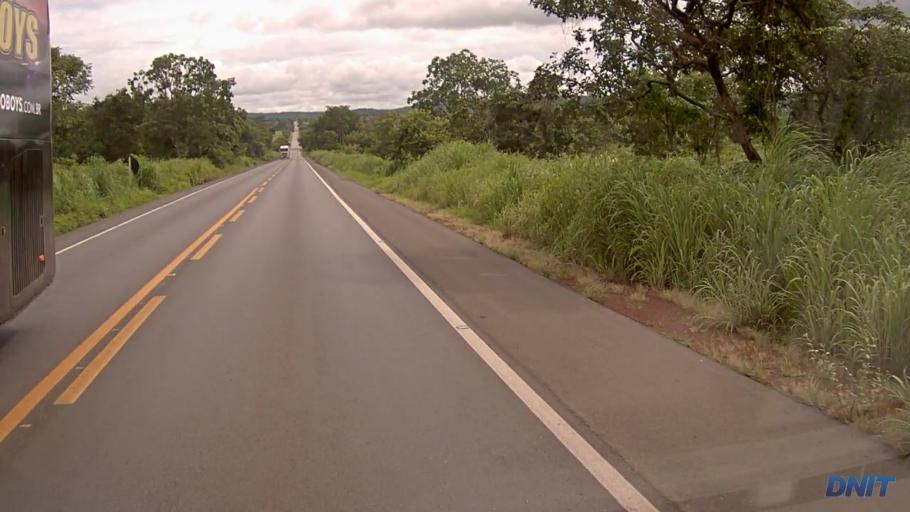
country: BR
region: Goias
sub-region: Posse
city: Posse
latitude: -14.4082
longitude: -46.4525
